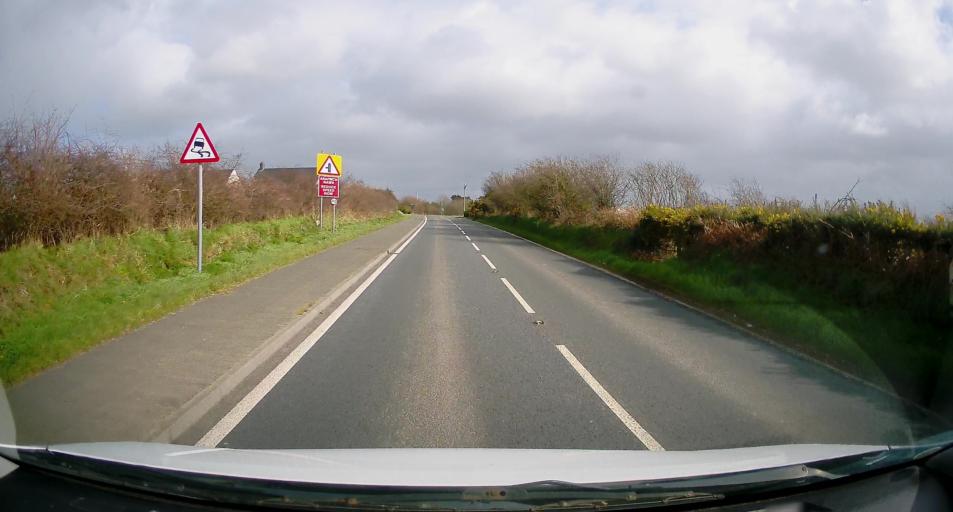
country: GB
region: Wales
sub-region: County of Ceredigion
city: Aberporth
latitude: 52.1117
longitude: -4.5525
